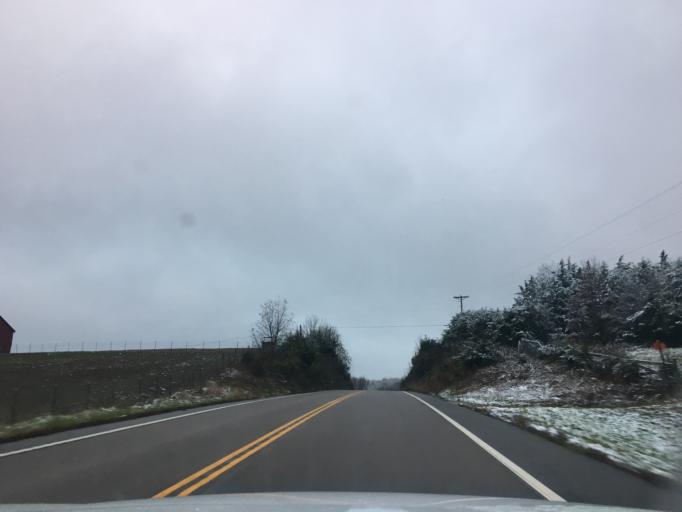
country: US
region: Missouri
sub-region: Osage County
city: Linn
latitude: 38.4685
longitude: -91.7695
